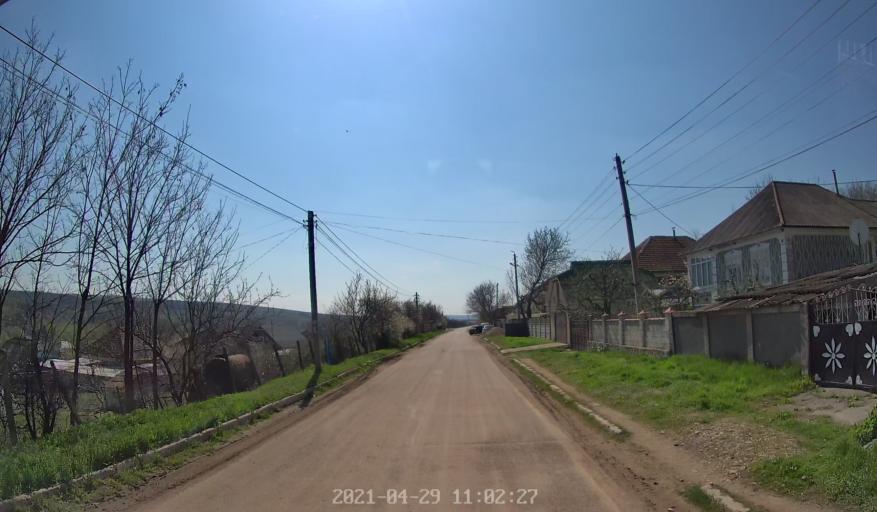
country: MD
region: Chisinau
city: Ciorescu
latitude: 47.1629
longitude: 28.9517
